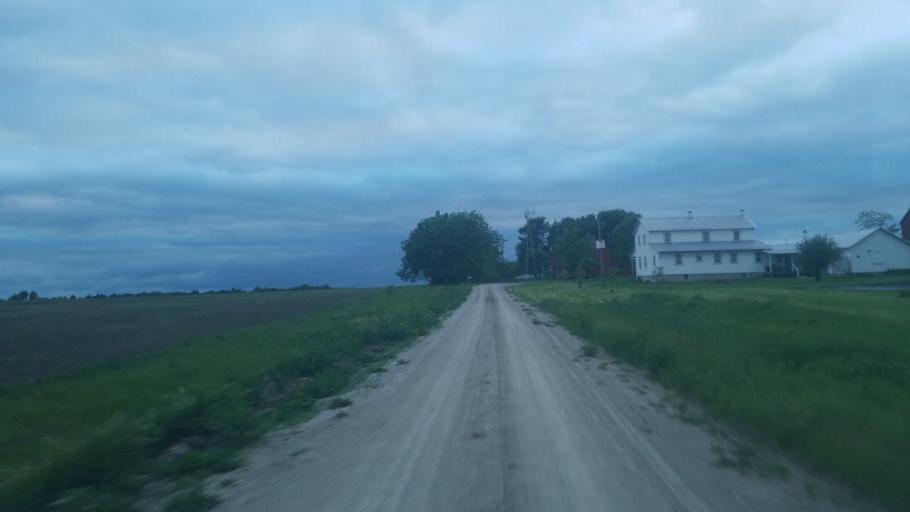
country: US
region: Iowa
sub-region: Decatur County
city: Lamoni
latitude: 40.5947
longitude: -93.9683
